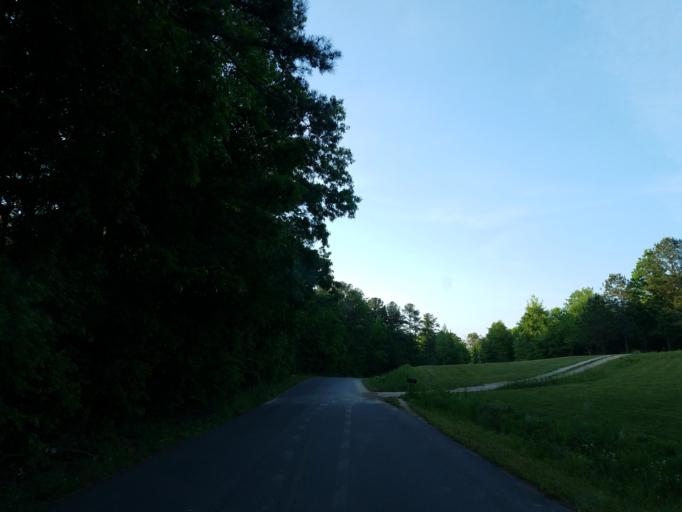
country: US
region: Georgia
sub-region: Whitfield County
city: Dalton
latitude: 34.6635
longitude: -85.0798
